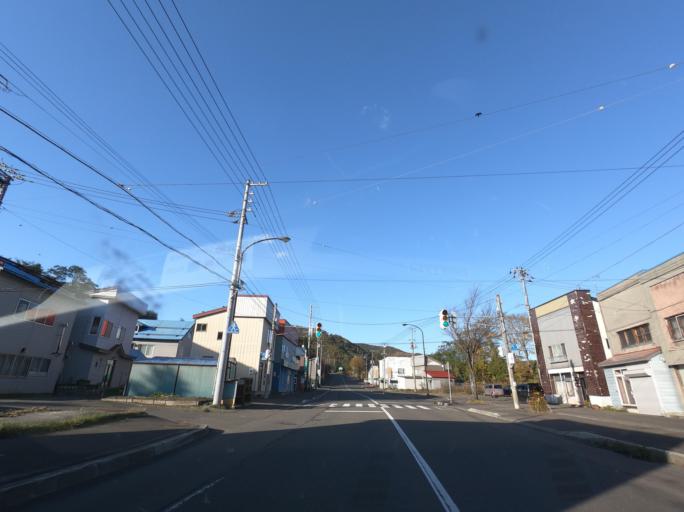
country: JP
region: Hokkaido
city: Iwamizawa
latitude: 43.0420
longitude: 141.9627
